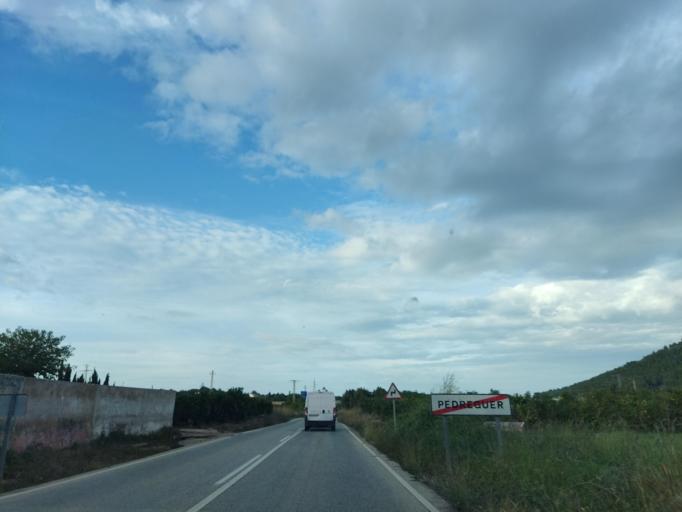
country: ES
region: Valencia
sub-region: Provincia de Alicante
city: Pedreguer
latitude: 38.8019
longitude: 0.0328
